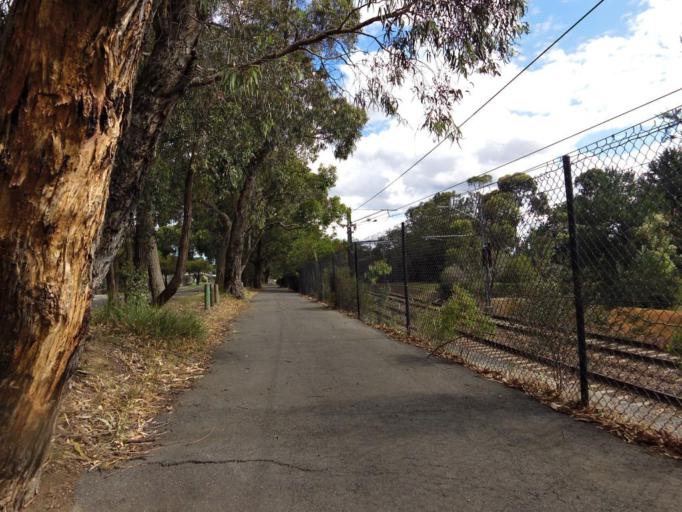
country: AU
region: Victoria
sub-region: Knox
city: Boronia
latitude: -37.8649
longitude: 145.2865
